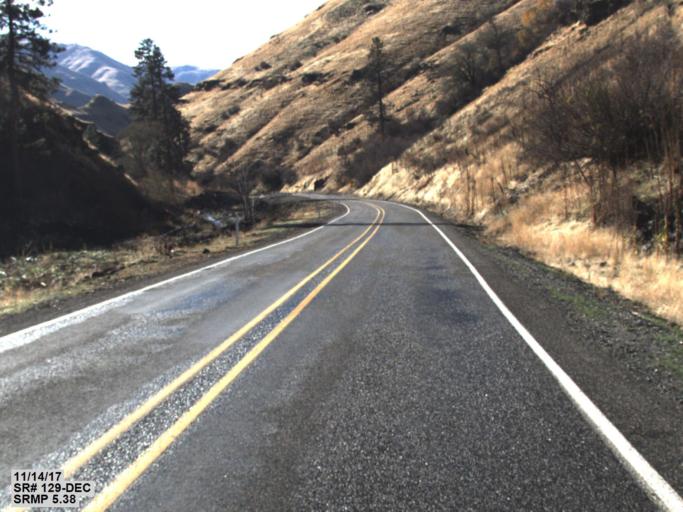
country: US
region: Washington
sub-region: Asotin County
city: Asotin
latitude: 46.0519
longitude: -117.2402
